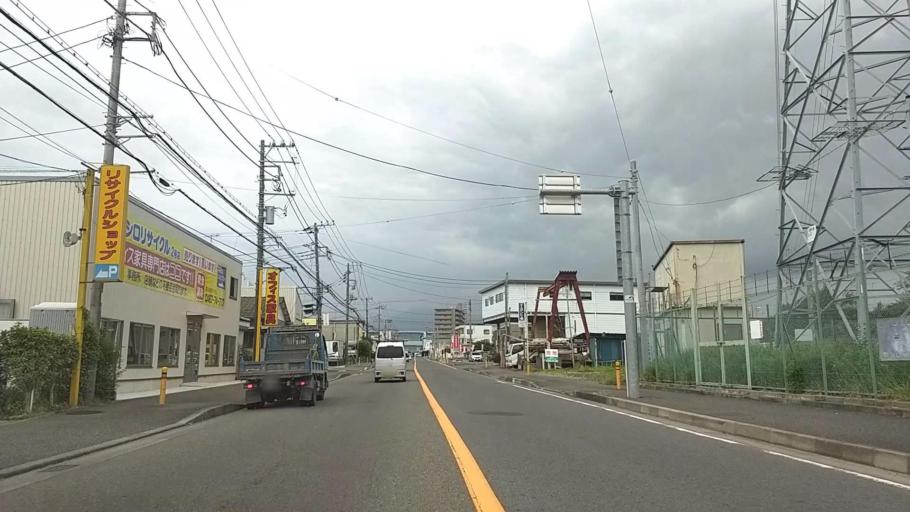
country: JP
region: Kanagawa
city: Chigasaki
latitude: 35.3705
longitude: 139.3801
